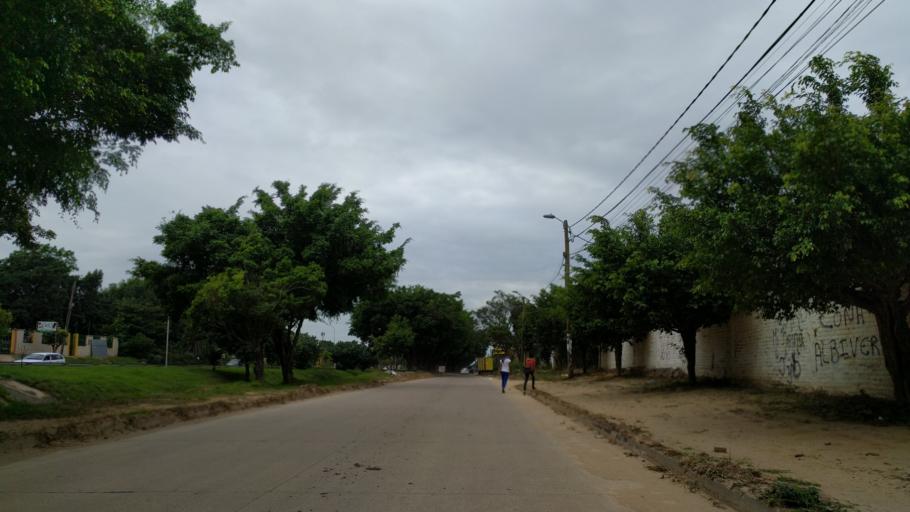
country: BO
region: Santa Cruz
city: Santa Cruz de la Sierra
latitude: -17.8147
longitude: -63.2289
